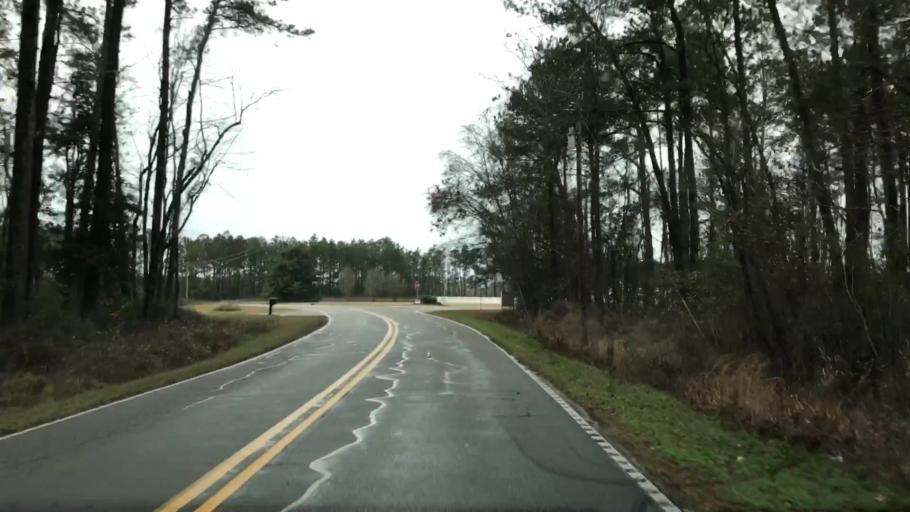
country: US
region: South Carolina
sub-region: Florence County
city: Johnsonville
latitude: 33.6684
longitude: -79.3122
